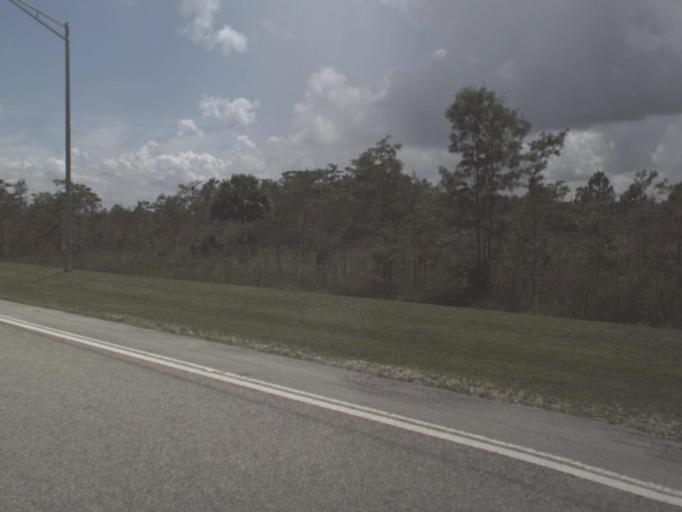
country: US
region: Florida
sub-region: Collier County
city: Immokalee
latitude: 26.1670
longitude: -81.1921
